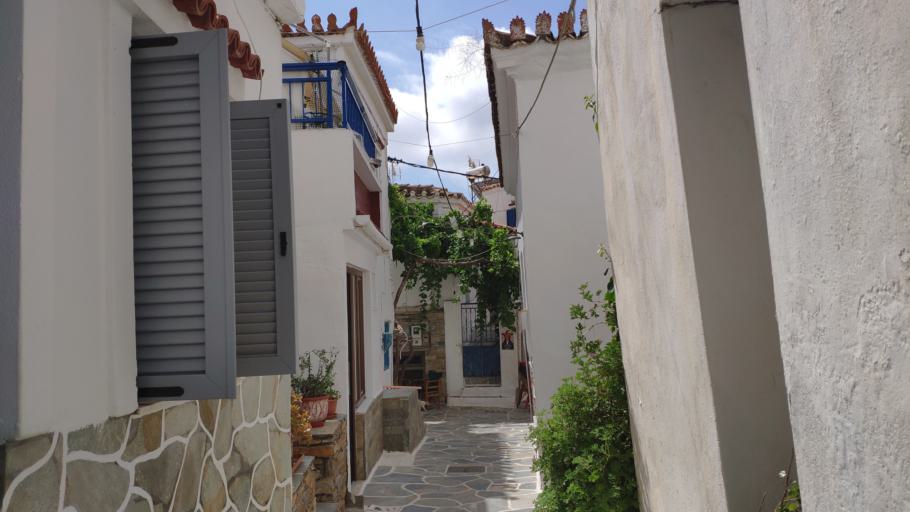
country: GR
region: South Aegean
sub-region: Nomos Kykladon
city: Kythnos
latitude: 37.3831
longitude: 24.4306
